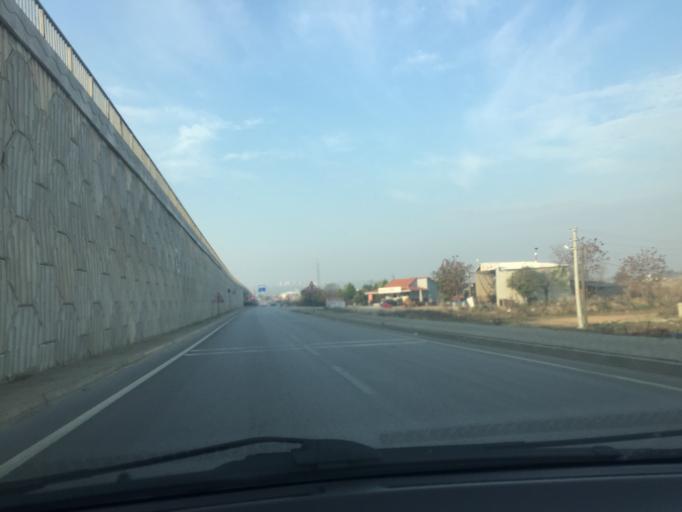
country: TR
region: Canakkale
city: Biga
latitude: 40.2416
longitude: 27.2597
